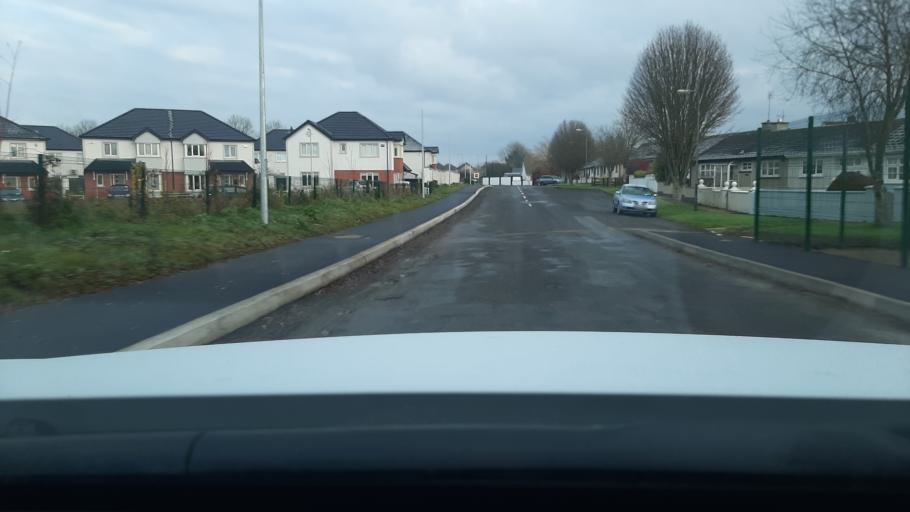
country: IE
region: Leinster
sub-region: Kildare
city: Rathangan
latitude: 53.2230
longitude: -7.0034
